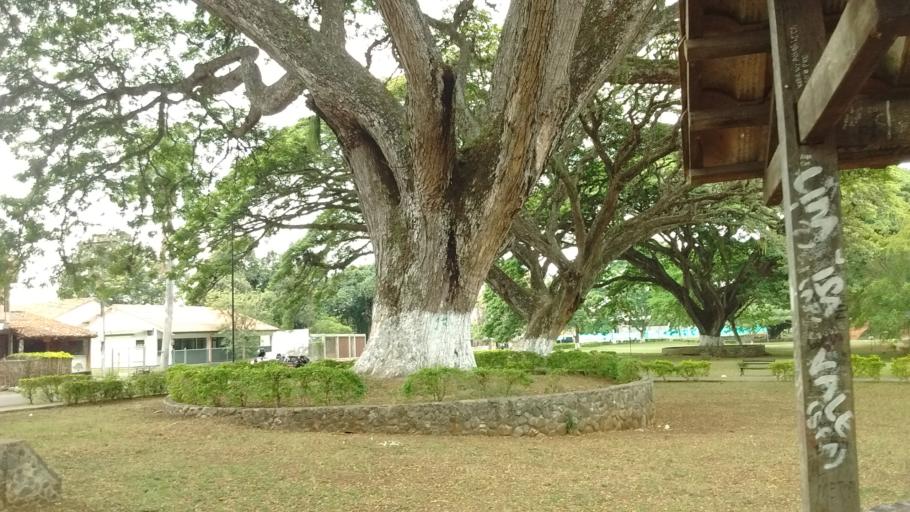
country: CO
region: Cauca
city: Caloto
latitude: 3.0338
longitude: -76.4067
